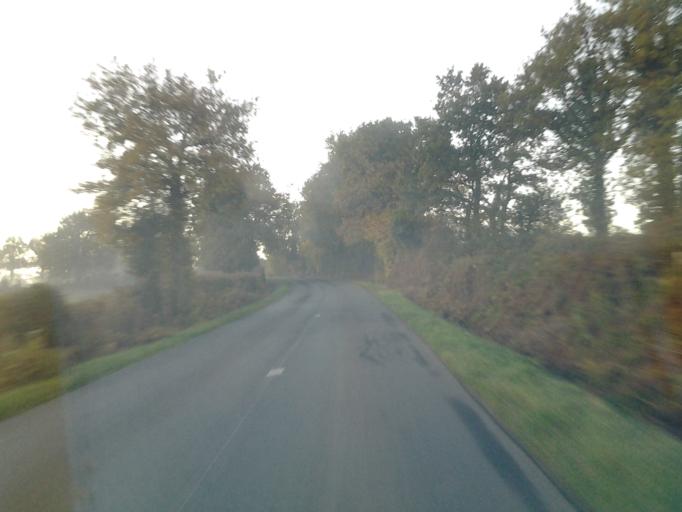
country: FR
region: Pays de la Loire
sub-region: Departement de la Vendee
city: Chateau-Guibert
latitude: 46.6278
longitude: -1.2333
